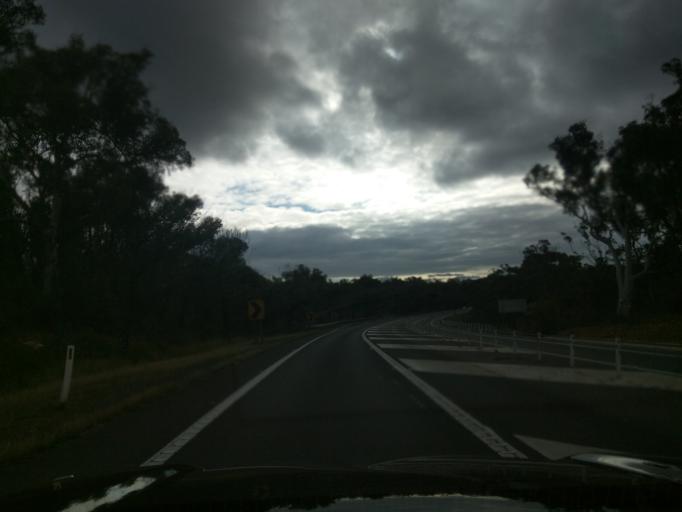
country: AU
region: New South Wales
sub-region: Wollondilly
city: Douglas Park
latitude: -34.3102
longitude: 150.7404
